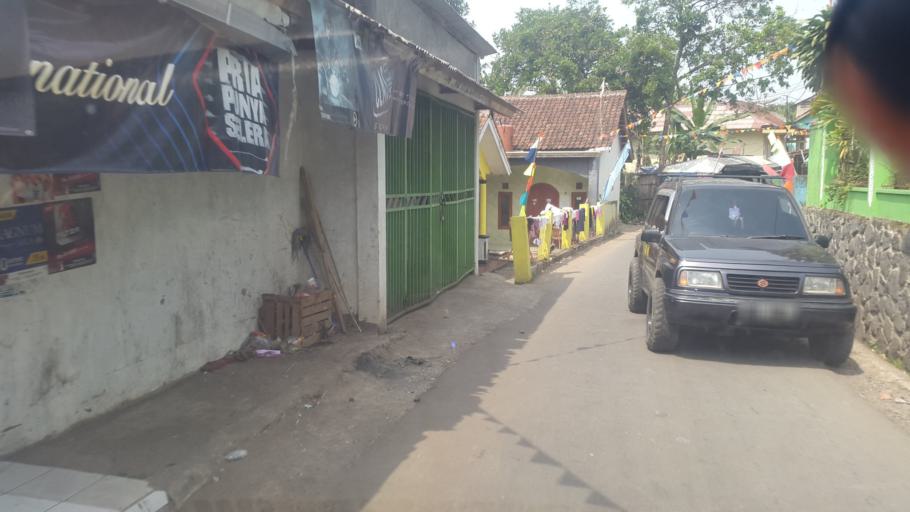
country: ID
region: West Java
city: Cicurug
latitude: -6.7614
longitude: 106.7521
